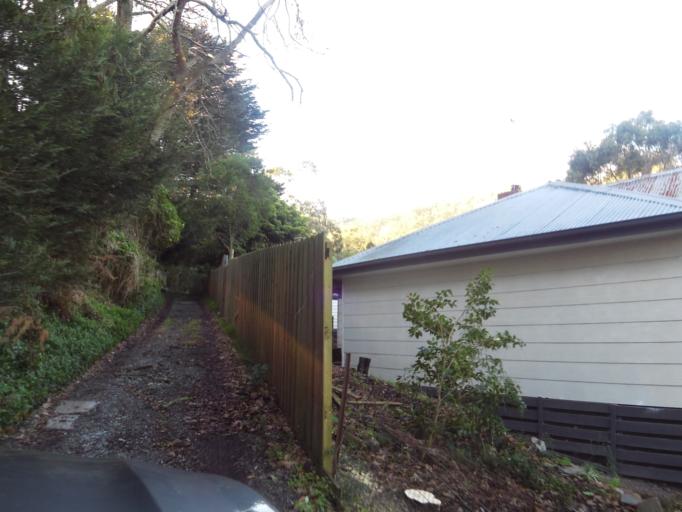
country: AU
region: Victoria
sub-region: Knox
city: Ferntree Gully
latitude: -37.8905
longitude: 145.3059
